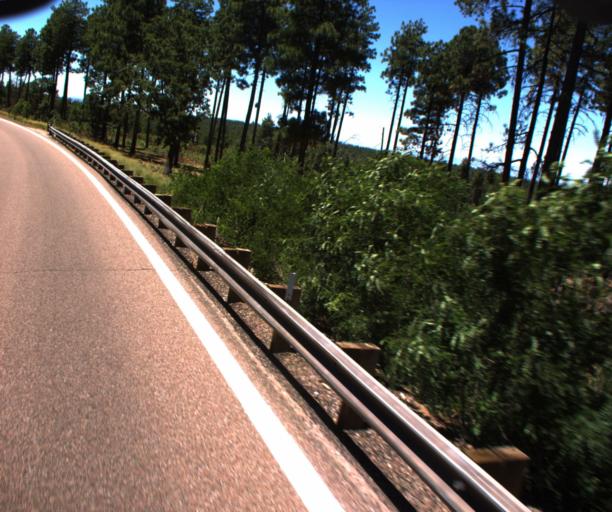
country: US
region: Arizona
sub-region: Gila County
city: Pine
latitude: 34.4437
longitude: -111.4644
